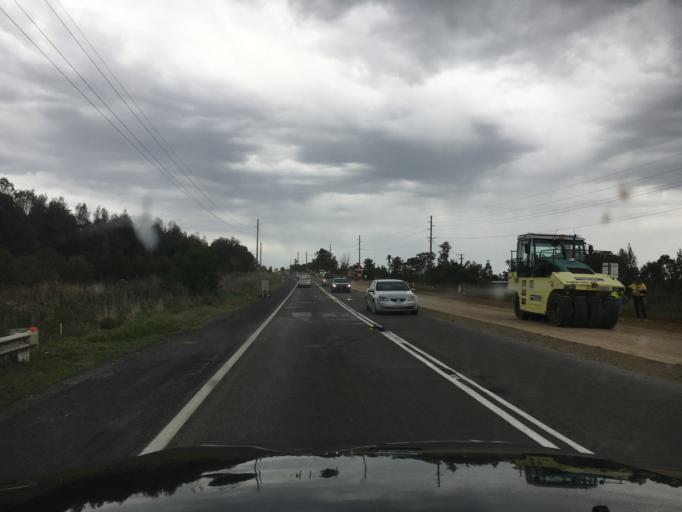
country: AU
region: New South Wales
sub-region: Muswellbrook
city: Muswellbrook
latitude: -32.1995
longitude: 150.8930
